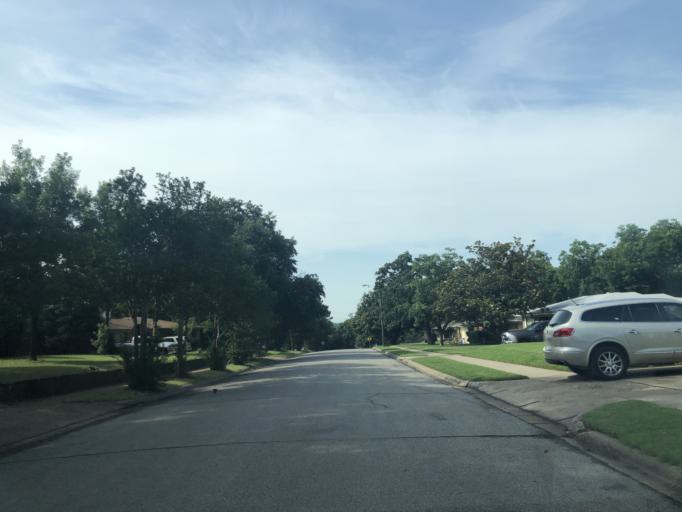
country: US
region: Texas
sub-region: Dallas County
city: Irving
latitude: 32.7988
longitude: -96.9626
